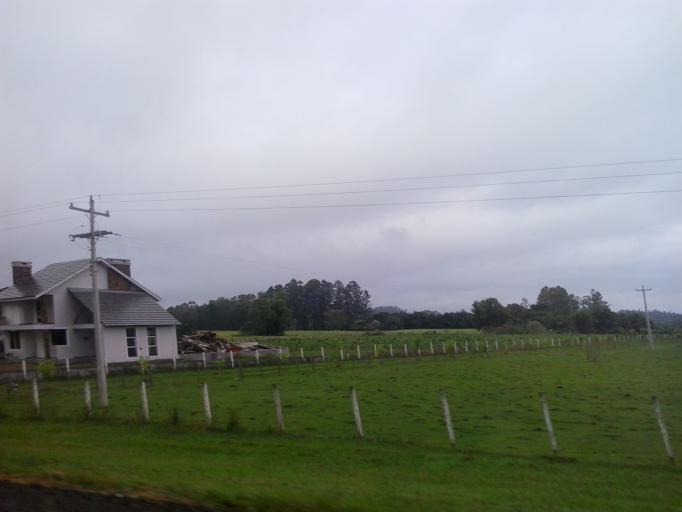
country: BR
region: Rio Grande do Sul
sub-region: Candelaria
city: Candelaria
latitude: -29.7154
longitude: -53.2459
